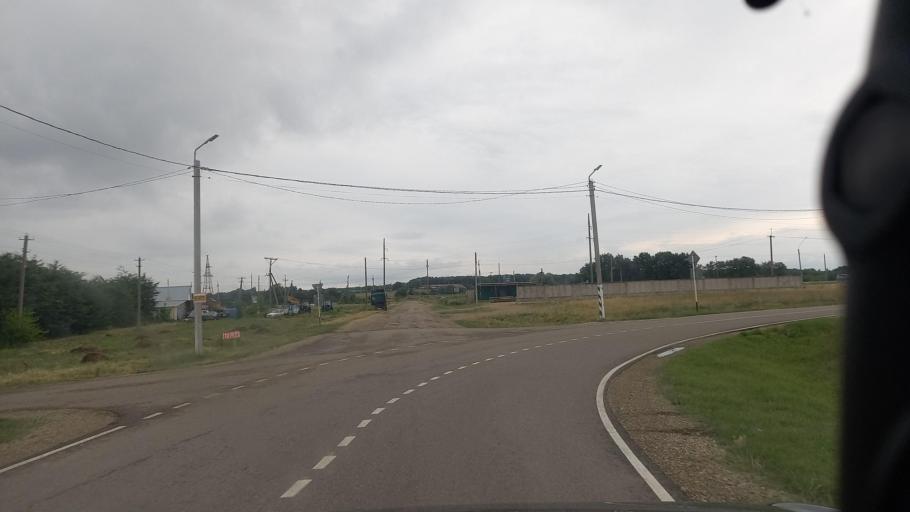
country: RU
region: Adygeya
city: Ponezhukay
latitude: 44.8797
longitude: 39.3942
